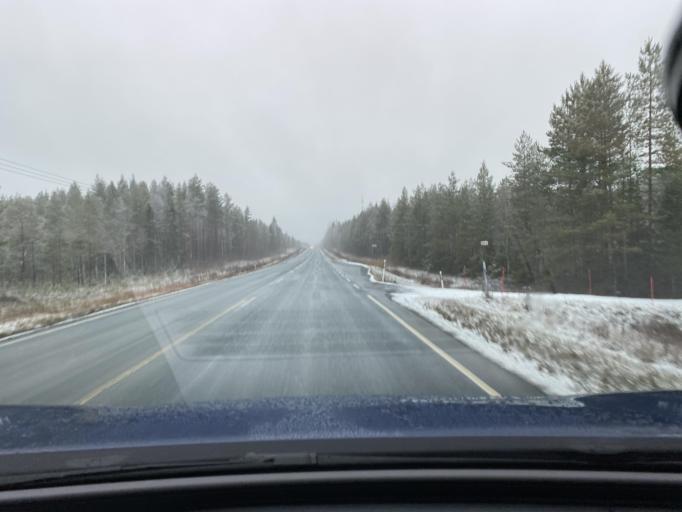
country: FI
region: Northern Ostrobothnia
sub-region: Oulu
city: Kiiminki
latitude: 65.1384
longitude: 25.8436
